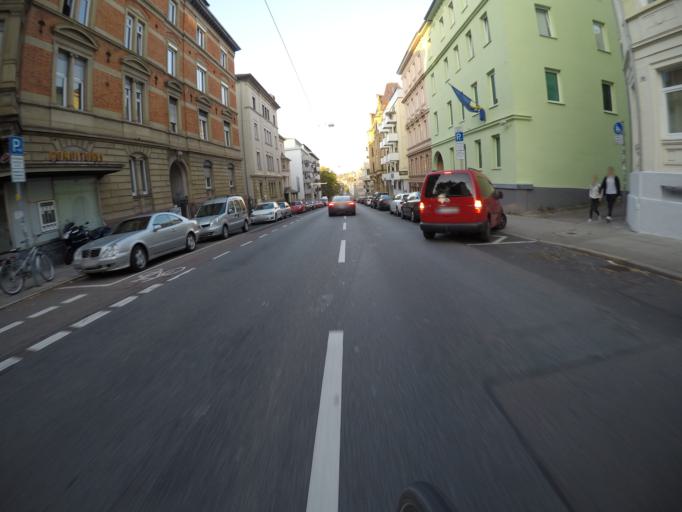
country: DE
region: Baden-Wuerttemberg
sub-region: Regierungsbezirk Stuttgart
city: Stuttgart
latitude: 48.7680
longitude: 9.1792
